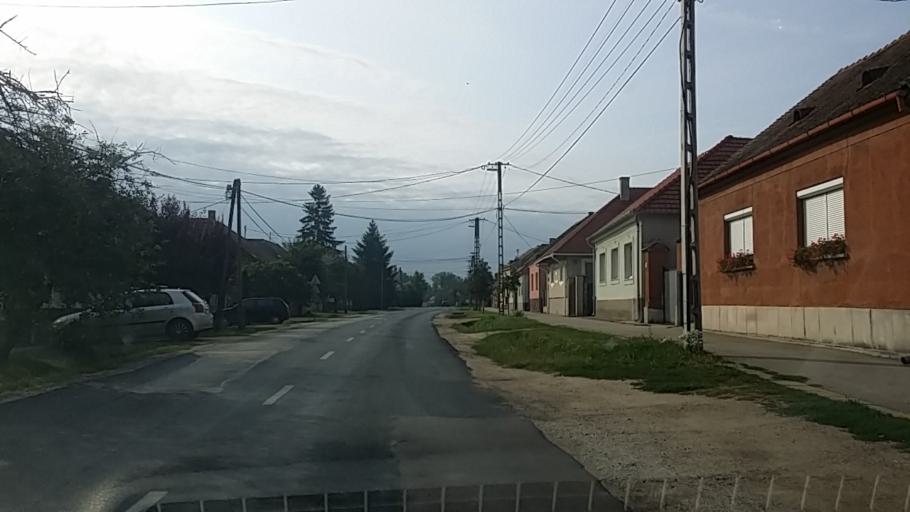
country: HU
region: Gyor-Moson-Sopron
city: Fertoszentmiklos
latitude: 47.6065
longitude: 16.9060
